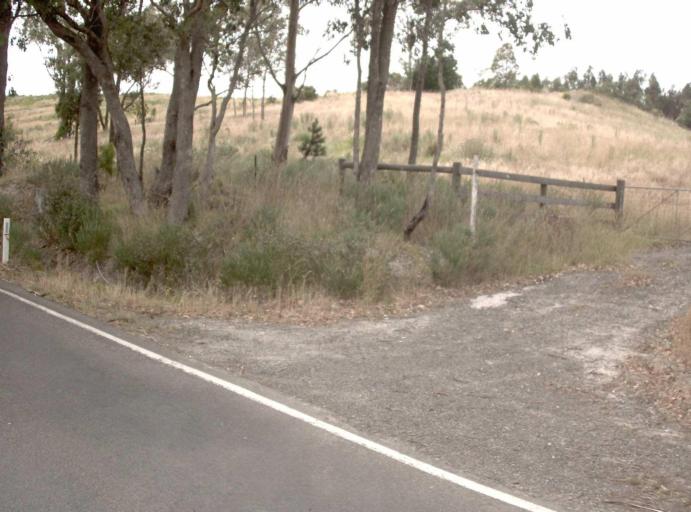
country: AU
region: Victoria
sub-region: Latrobe
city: Traralgon
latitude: -38.1418
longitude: 146.4843
